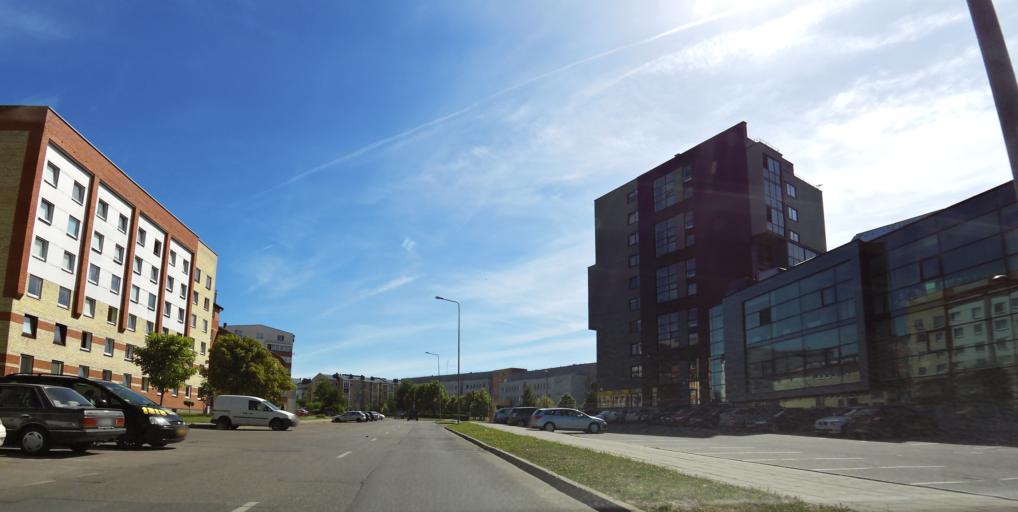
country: LT
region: Vilnius County
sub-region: Vilnius
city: Fabijoniskes
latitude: 54.7234
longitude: 25.2351
